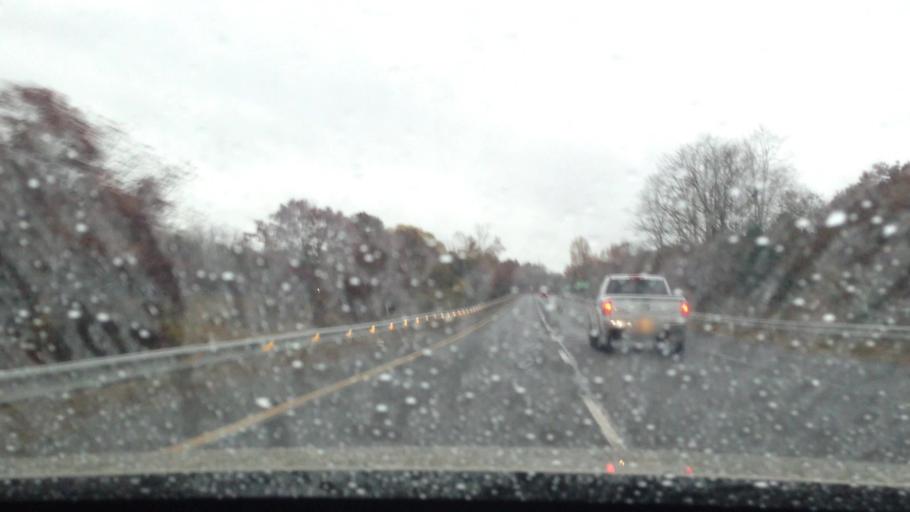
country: US
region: New York
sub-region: Suffolk County
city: Selden
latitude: 40.8546
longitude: -73.0206
